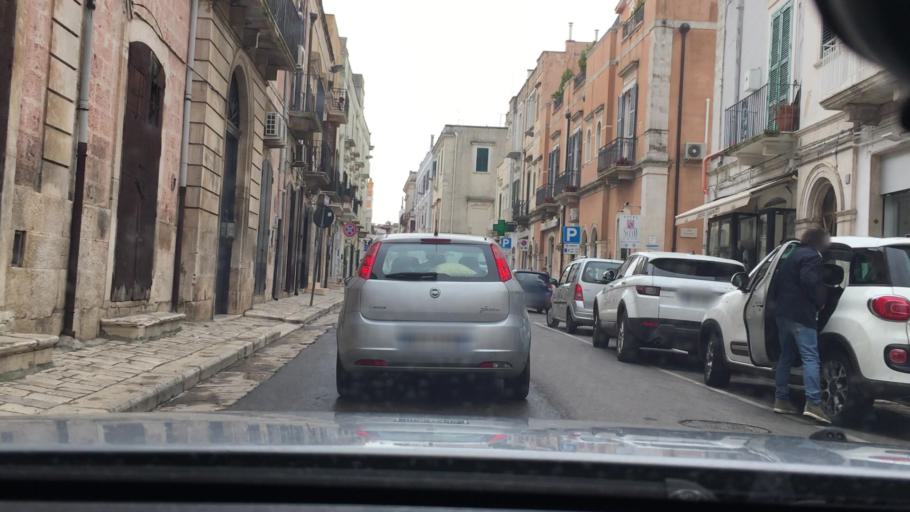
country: IT
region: Apulia
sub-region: Provincia di Bari
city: Gioia del Colle
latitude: 40.8003
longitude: 16.9212
